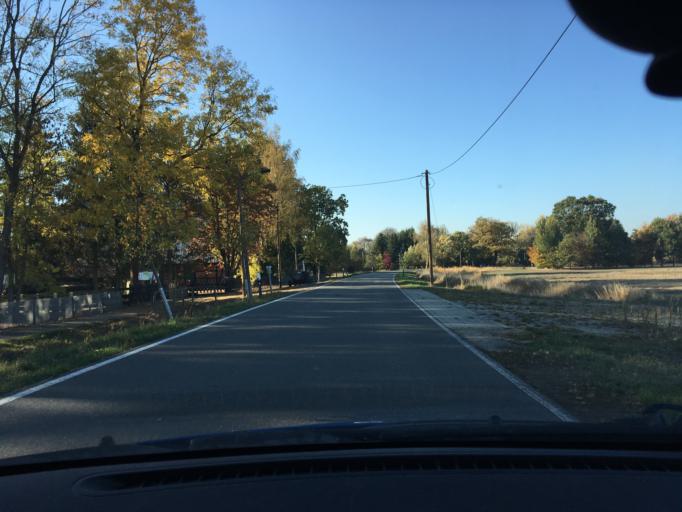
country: DE
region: Lower Saxony
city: Hitzacker
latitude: 53.1675
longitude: 11.0379
